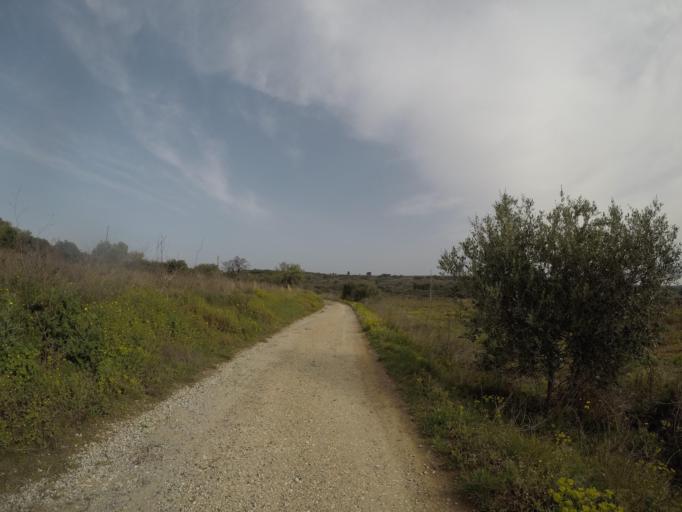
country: FR
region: Languedoc-Roussillon
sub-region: Departement des Pyrenees-Orientales
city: Baixas
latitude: 42.7620
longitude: 2.8186
